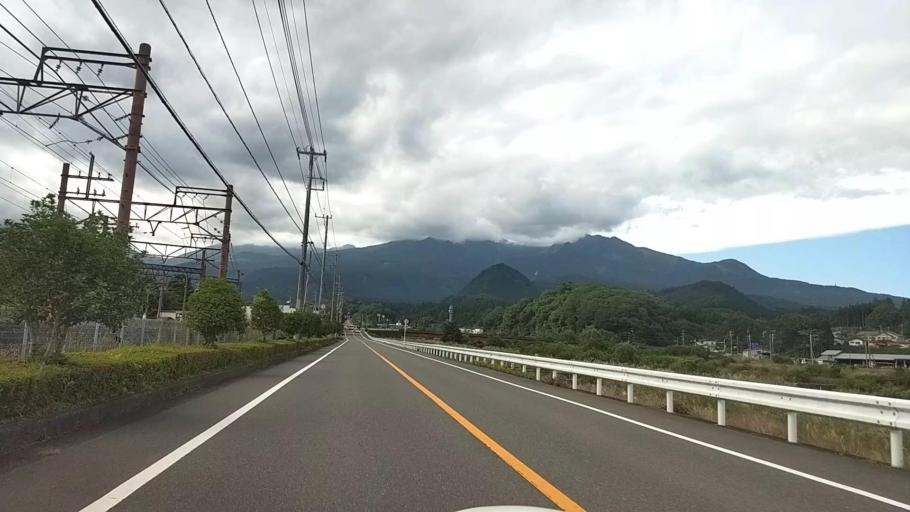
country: JP
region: Tochigi
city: Nikko
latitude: 36.7480
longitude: 139.6226
